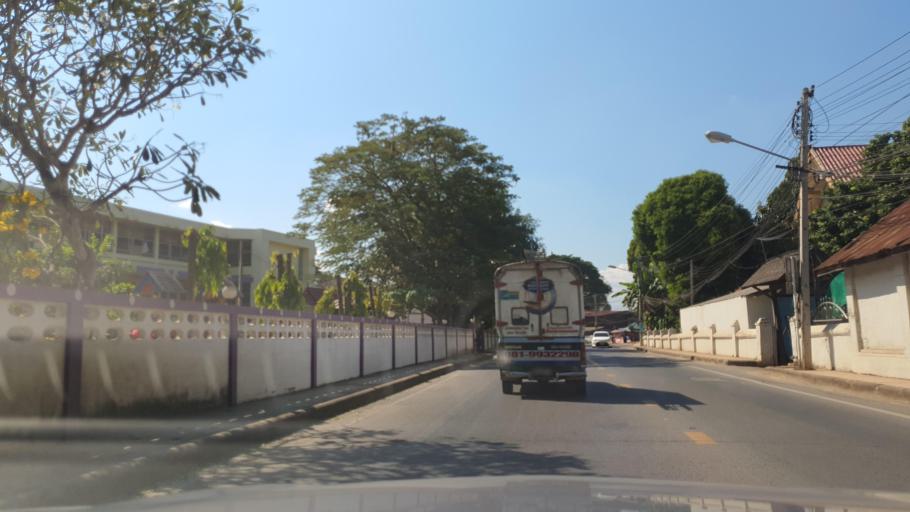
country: TH
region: Nan
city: Nan
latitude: 18.7837
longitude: 100.7743
